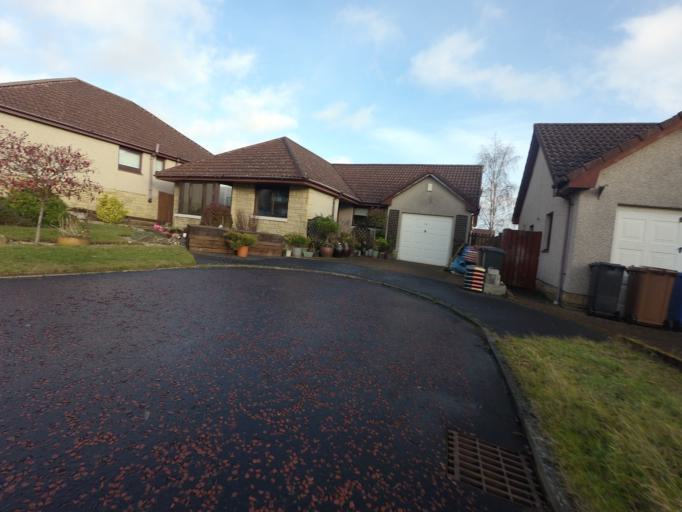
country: GB
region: Scotland
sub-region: West Lothian
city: West Calder
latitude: 55.8790
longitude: -3.5840
